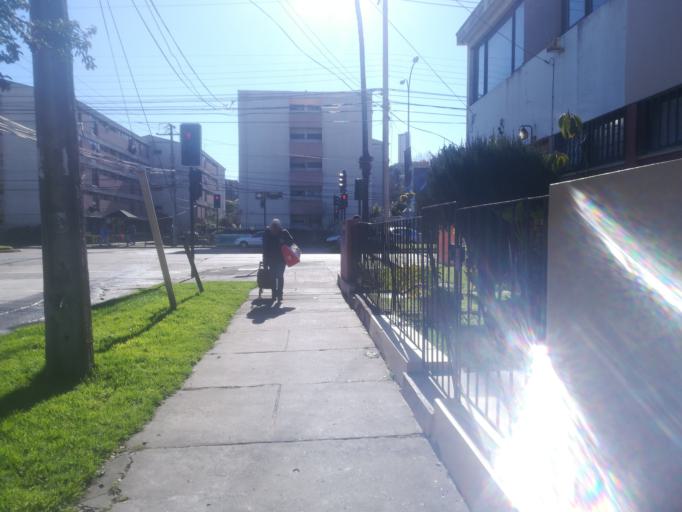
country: CL
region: Valparaiso
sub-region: Provincia de Valparaiso
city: Vina del Mar
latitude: -33.0091
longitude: -71.5435
